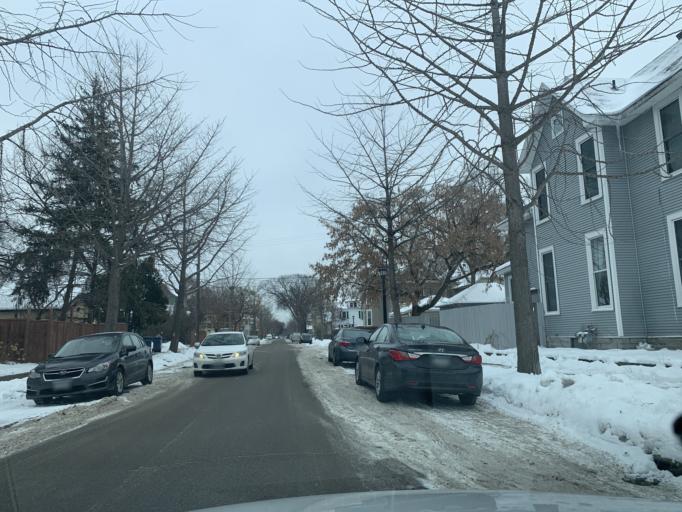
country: US
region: Minnesota
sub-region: Hennepin County
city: Minneapolis
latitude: 44.9538
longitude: -93.2957
